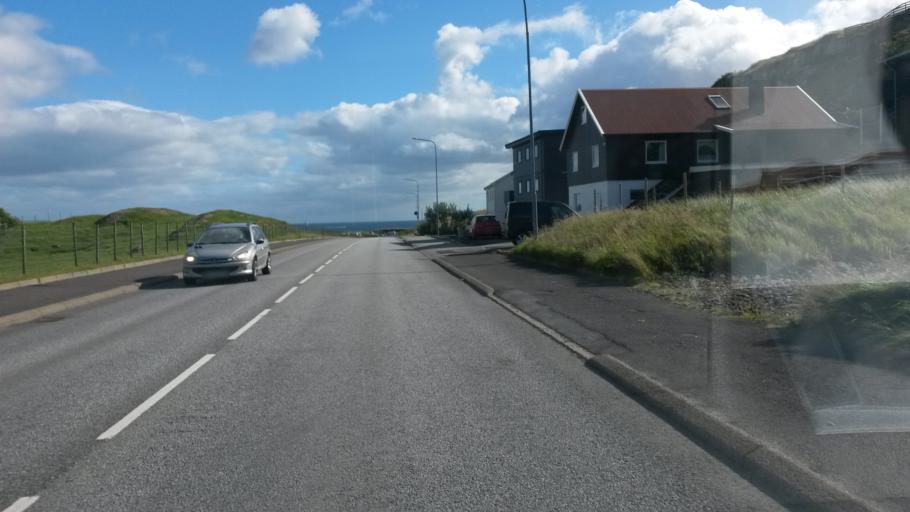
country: FO
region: Streymoy
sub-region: Torshavn
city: Torshavn
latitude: 62.0201
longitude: -6.7575
